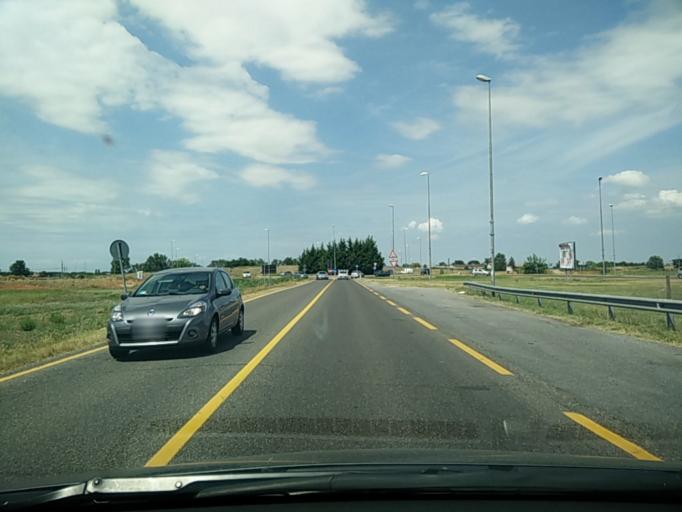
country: IT
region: Lombardy
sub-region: Provincia di Pavia
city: Torrazza Coste
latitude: 45.0009
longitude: 9.0691
